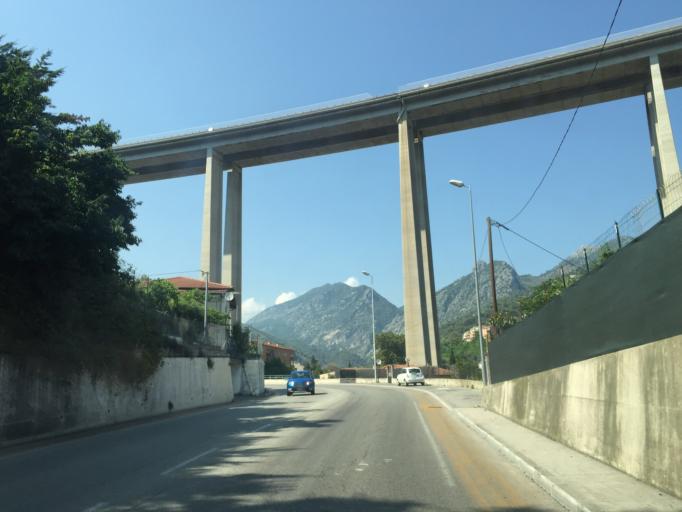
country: FR
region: Provence-Alpes-Cote d'Azur
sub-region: Departement des Alpes-Maritimes
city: Sainte-Agnes
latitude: 43.7957
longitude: 7.4894
